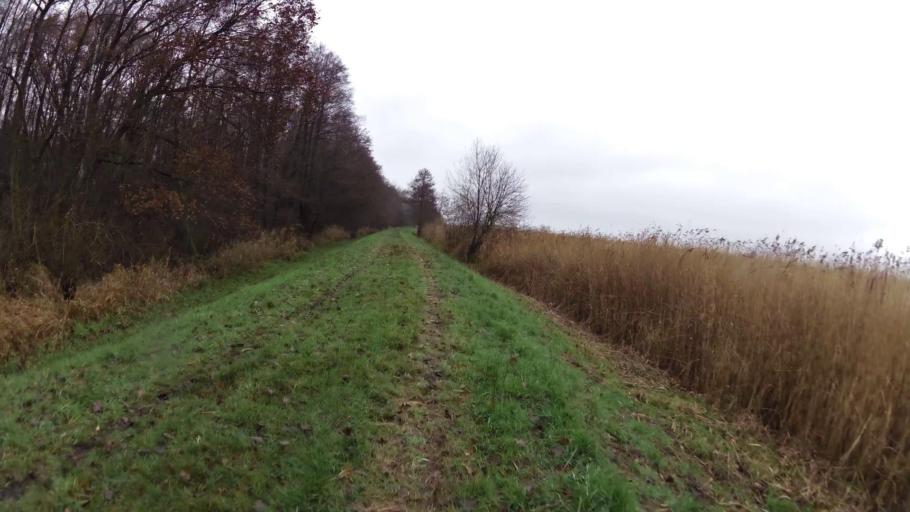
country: PL
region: West Pomeranian Voivodeship
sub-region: Powiat koszalinski
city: Mielno
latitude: 54.2527
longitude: 16.1238
